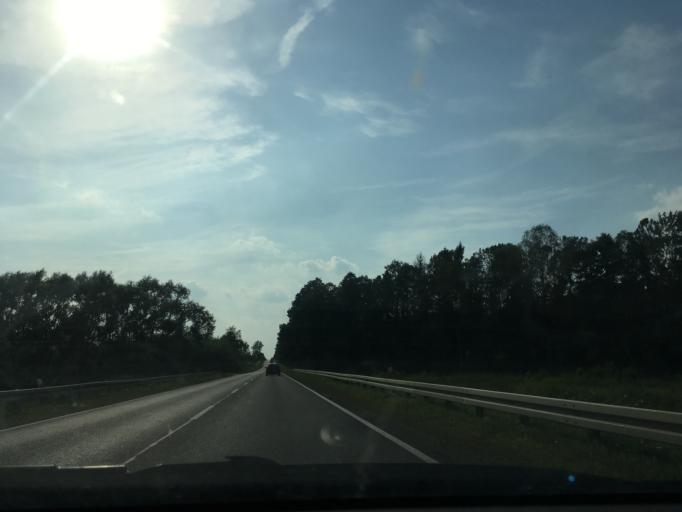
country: PL
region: Podlasie
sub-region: Powiat bialostocki
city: Suprasl
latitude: 53.1255
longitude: 23.2981
